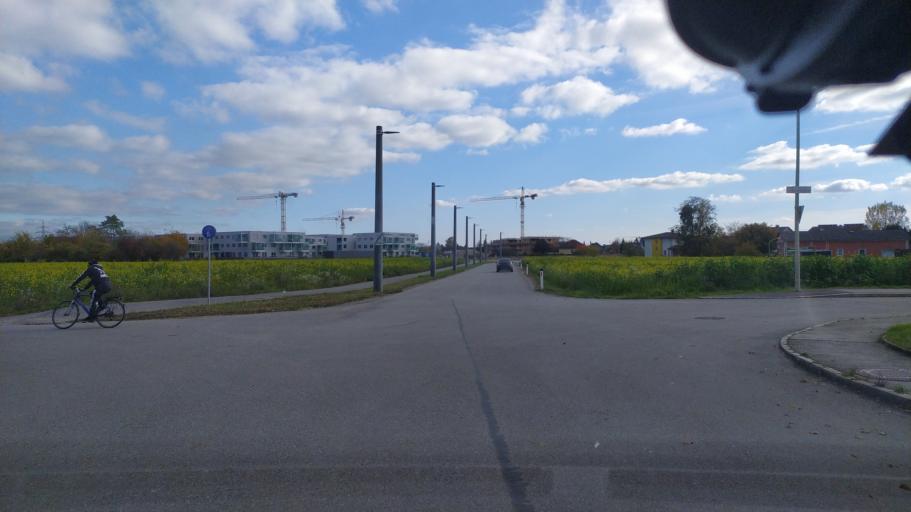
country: AT
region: Upper Austria
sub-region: Politischer Bezirk Urfahr-Umgebung
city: Steyregg
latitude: 48.2562
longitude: 14.3642
